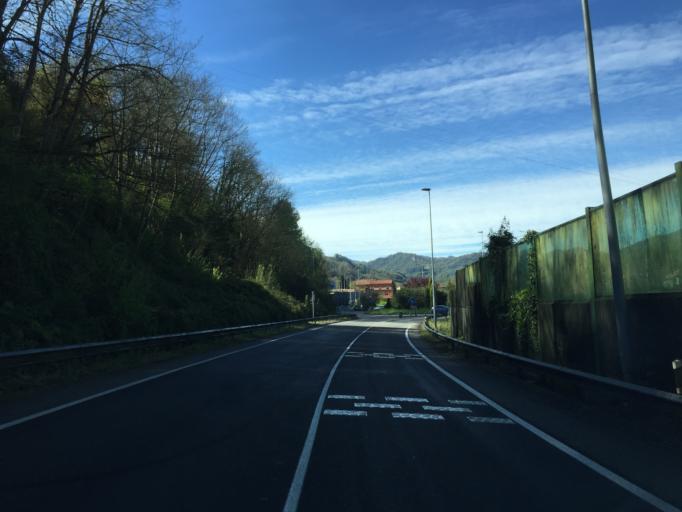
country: ES
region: Asturias
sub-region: Province of Asturias
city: Castandiello
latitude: 43.3547
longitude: -5.9611
